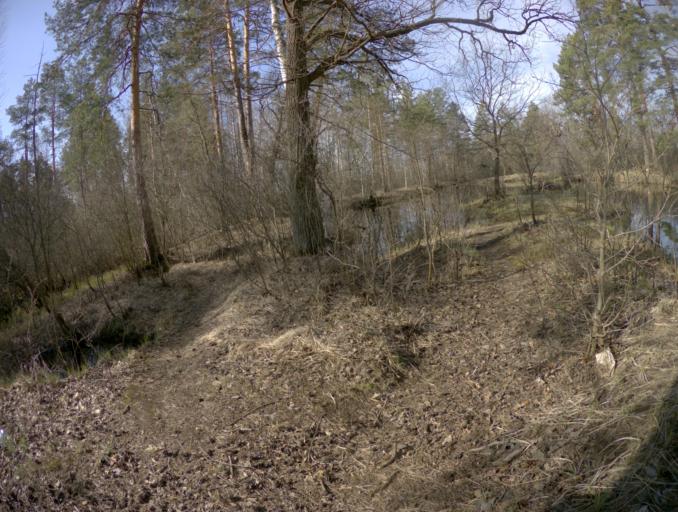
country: RU
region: Vladimir
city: Mezinovskiy
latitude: 55.5965
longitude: 40.3857
